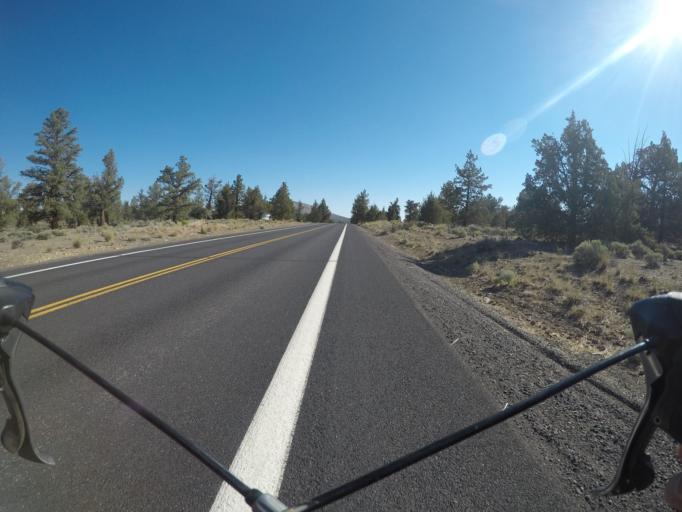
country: US
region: Oregon
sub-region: Deschutes County
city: Redmond
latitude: 44.2207
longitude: -121.3120
